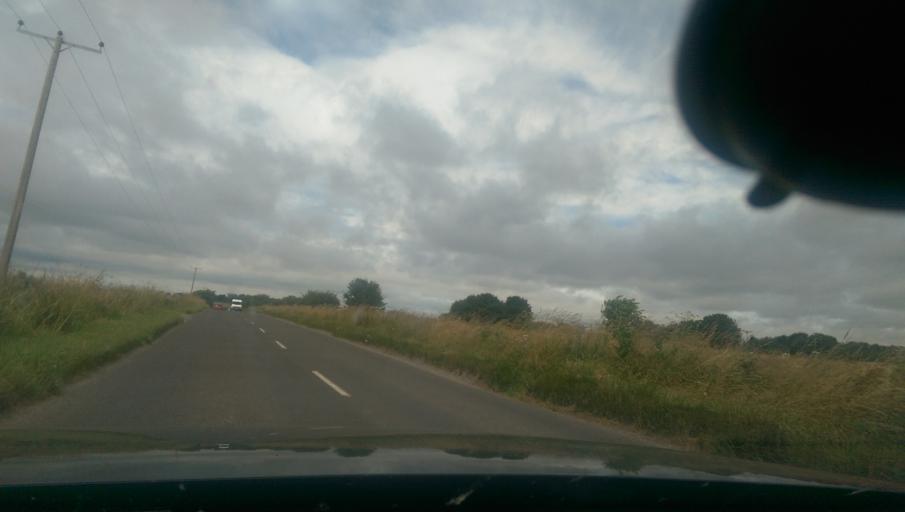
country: GB
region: England
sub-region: Wiltshire
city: Shrewton
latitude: 51.2000
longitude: -1.8419
